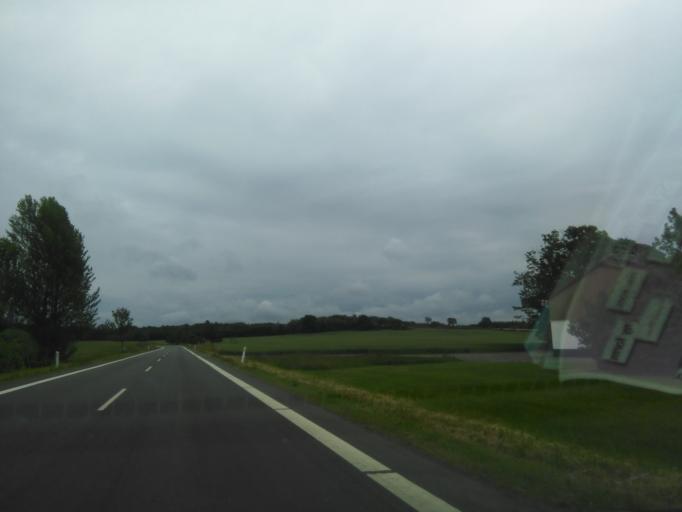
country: DK
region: Capital Region
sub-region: Bornholm Kommune
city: Akirkeby
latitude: 55.1173
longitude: 14.8291
